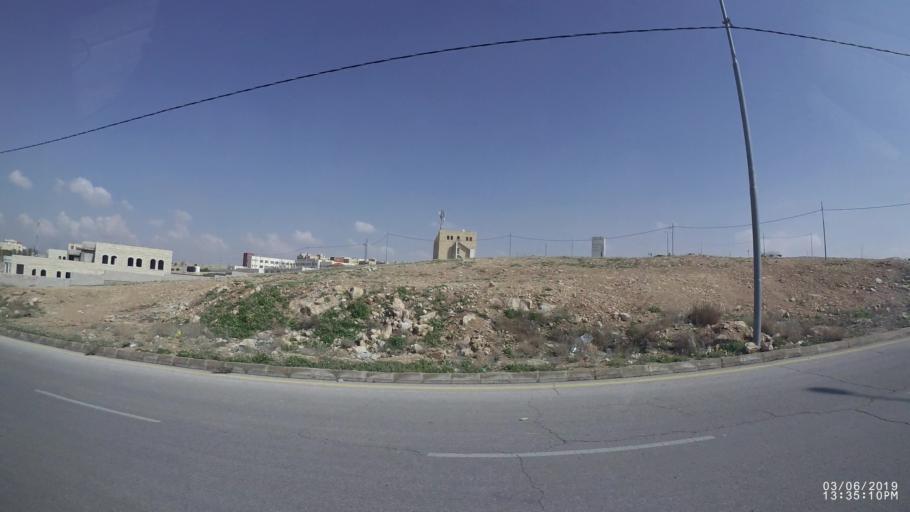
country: JO
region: Zarqa
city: Zarqa
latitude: 32.0750
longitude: 36.1075
